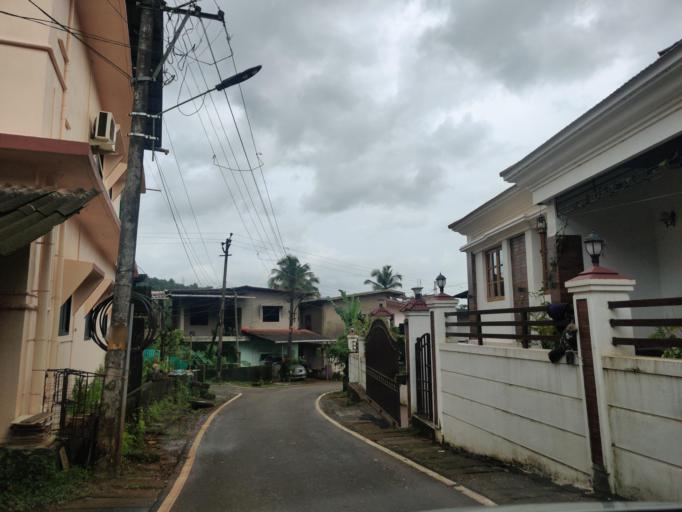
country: IN
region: Goa
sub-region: North Goa
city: Valpoy
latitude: 15.5265
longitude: 74.1421
